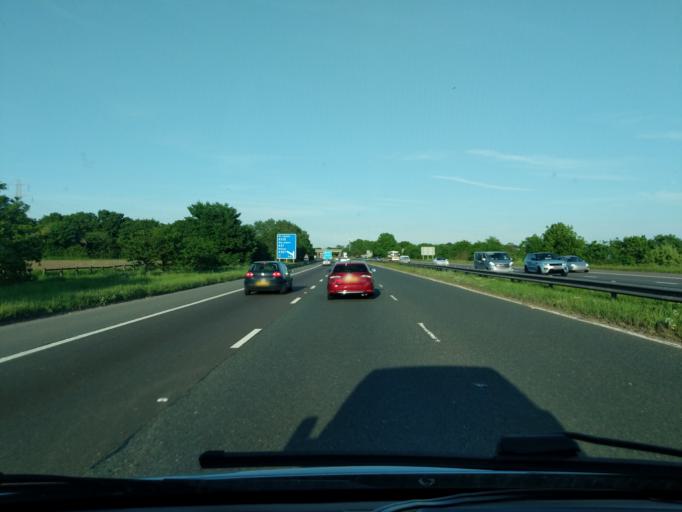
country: GB
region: England
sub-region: Knowsley
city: Whiston
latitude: 53.4007
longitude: -2.7742
